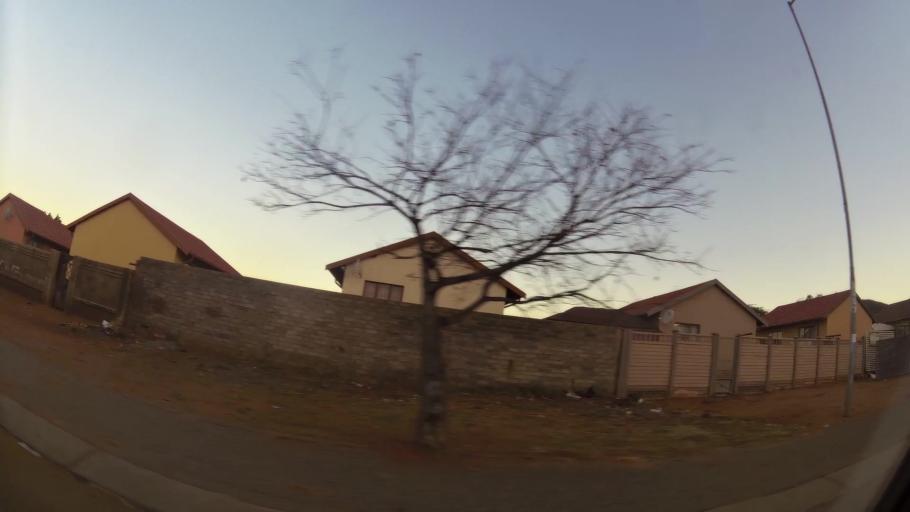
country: ZA
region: North-West
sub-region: Bojanala Platinum District Municipality
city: Rustenburg
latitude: -25.6511
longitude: 27.2043
